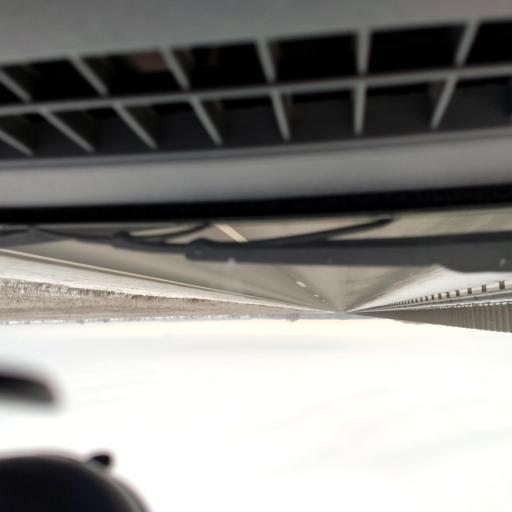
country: RU
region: Bashkortostan
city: Kushnarenkovo
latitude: 55.0609
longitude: 55.4029
